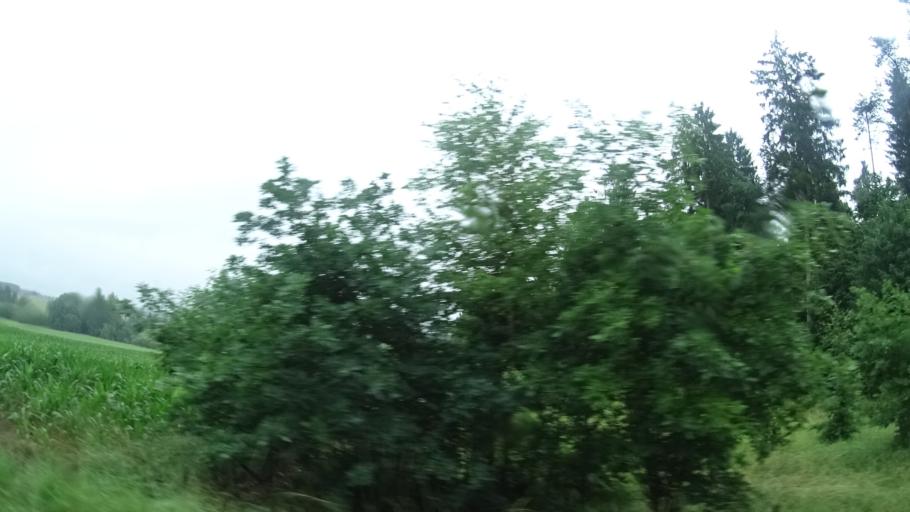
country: BE
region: Wallonia
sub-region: Province du Luxembourg
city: Saint-Leger
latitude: 49.6533
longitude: 5.6752
